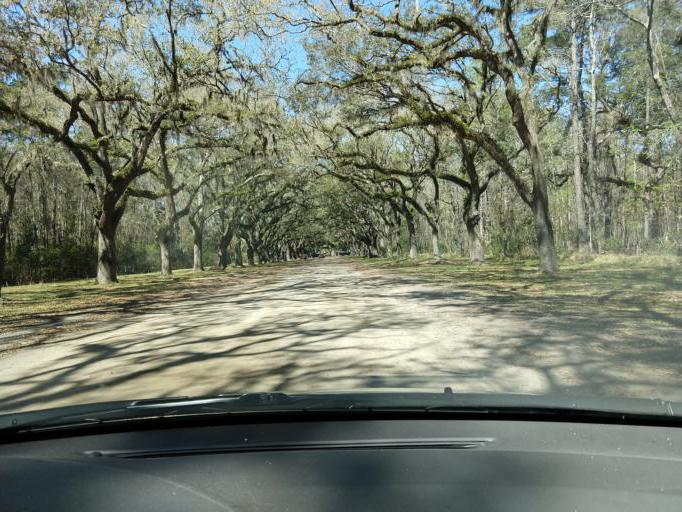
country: US
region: Georgia
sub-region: Chatham County
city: Isle of Hope
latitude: 31.9781
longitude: -81.0691
